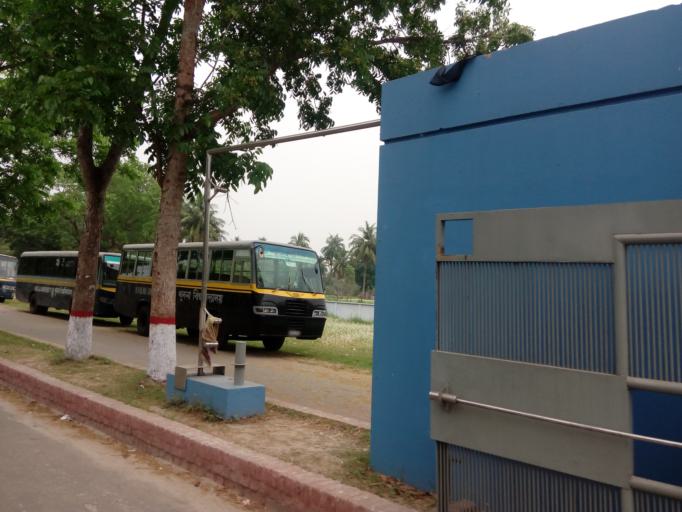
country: BD
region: Khulna
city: Khulna
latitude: 22.7997
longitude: 89.5345
